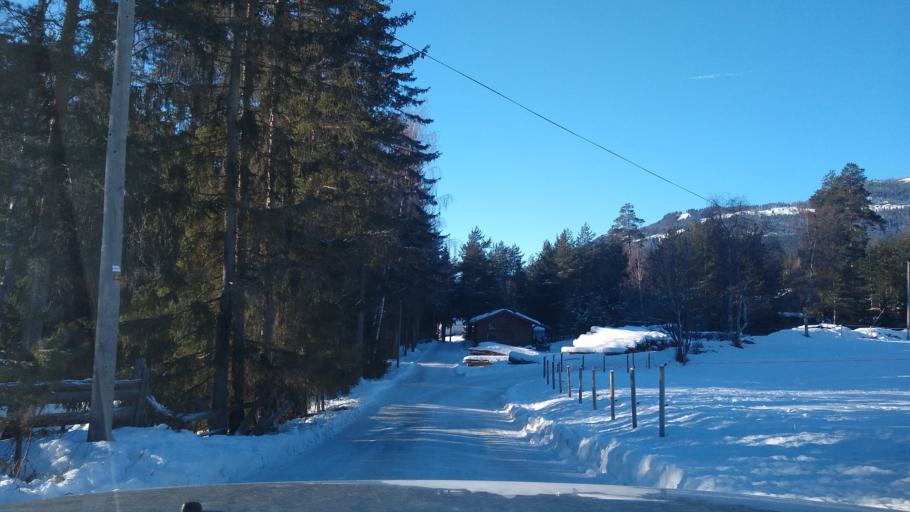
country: NO
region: Oppland
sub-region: Ringebu
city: Ringebu
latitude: 61.5505
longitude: 10.0728
